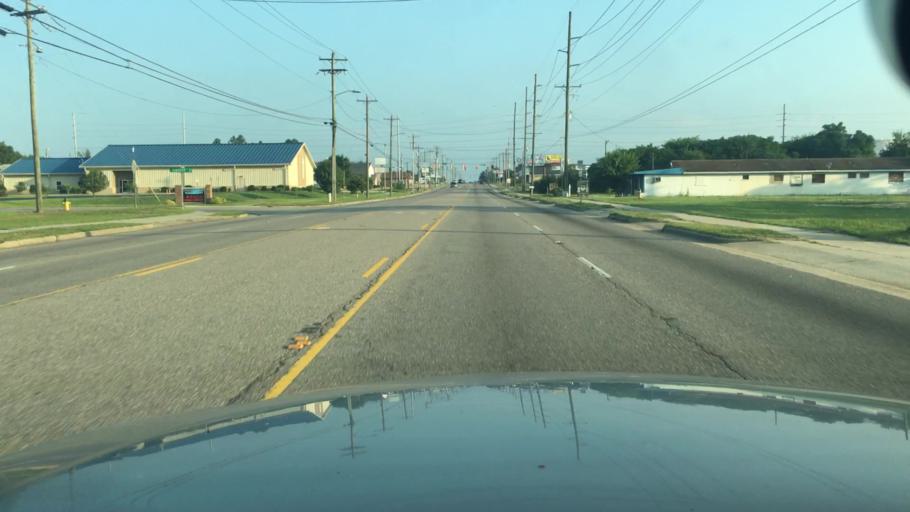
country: US
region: North Carolina
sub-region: Cumberland County
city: Spring Lake
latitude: 35.1098
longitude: -78.9262
